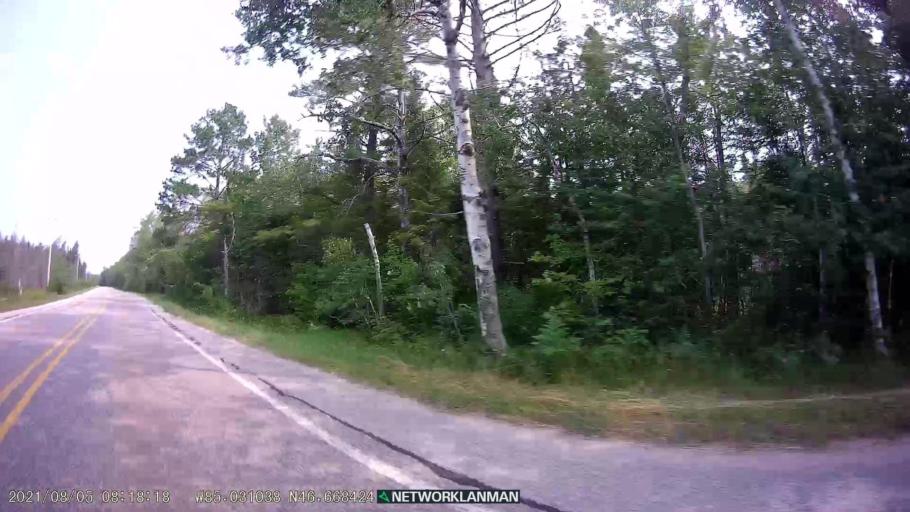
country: US
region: Michigan
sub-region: Luce County
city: Newberry
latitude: 46.6691
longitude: -85.0314
